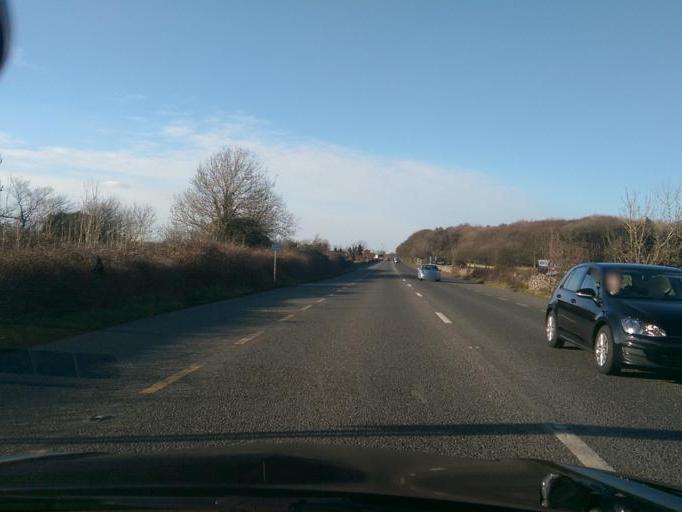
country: IE
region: Connaught
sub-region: County Galway
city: Oranmore
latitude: 53.2200
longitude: -8.8740
